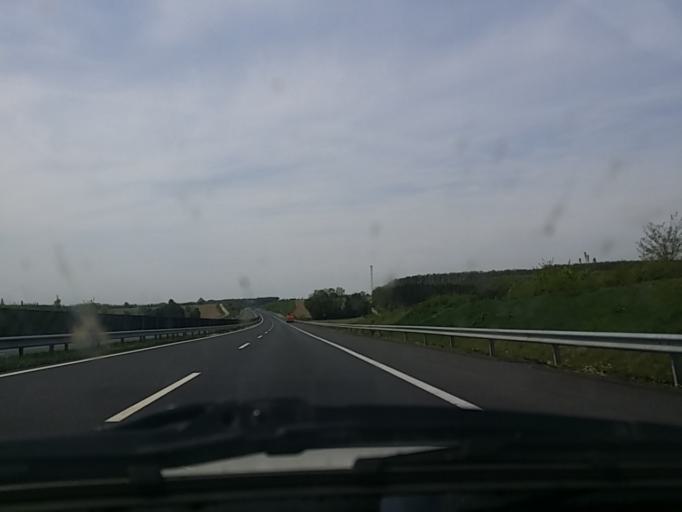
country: HU
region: Zala
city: Zalakomar
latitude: 46.4846
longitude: 17.0936
